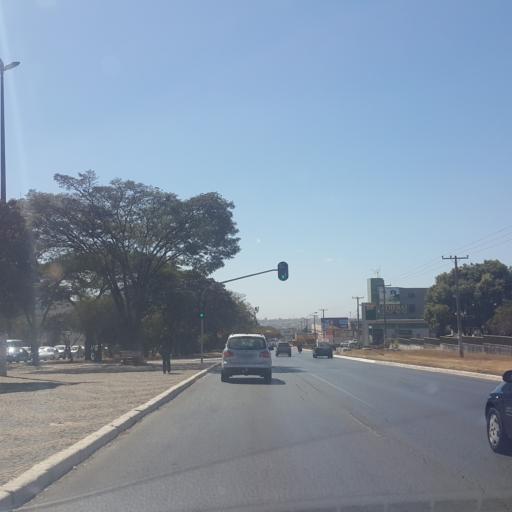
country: BR
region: Federal District
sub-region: Brasilia
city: Brasilia
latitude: -15.8136
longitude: -48.0972
